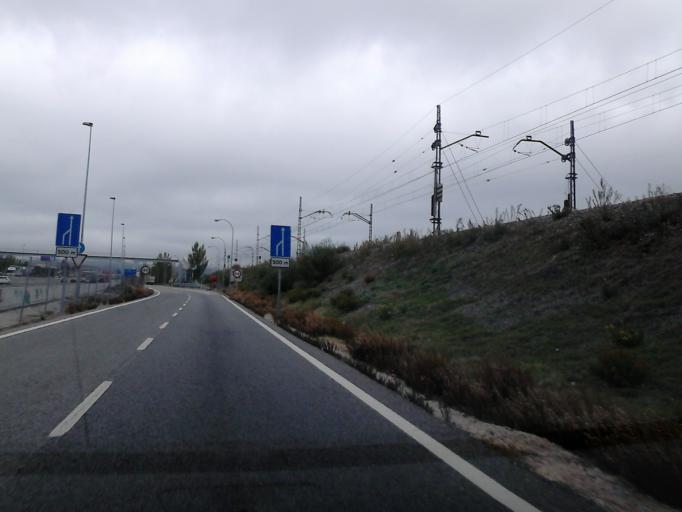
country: ES
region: Madrid
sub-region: Provincia de Madrid
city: Las Matas
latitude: 40.5359
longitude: -3.8889
